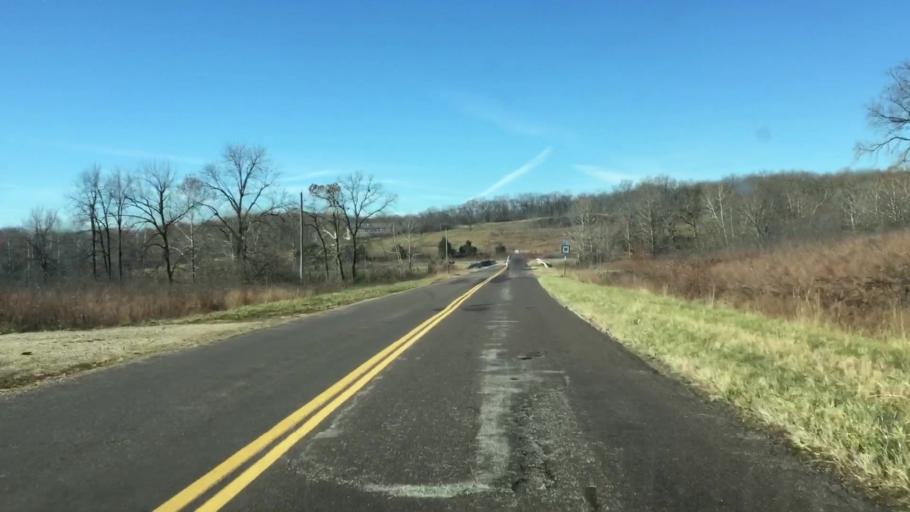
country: US
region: Missouri
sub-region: Miller County
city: Eldon
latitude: 38.3384
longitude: -92.7175
